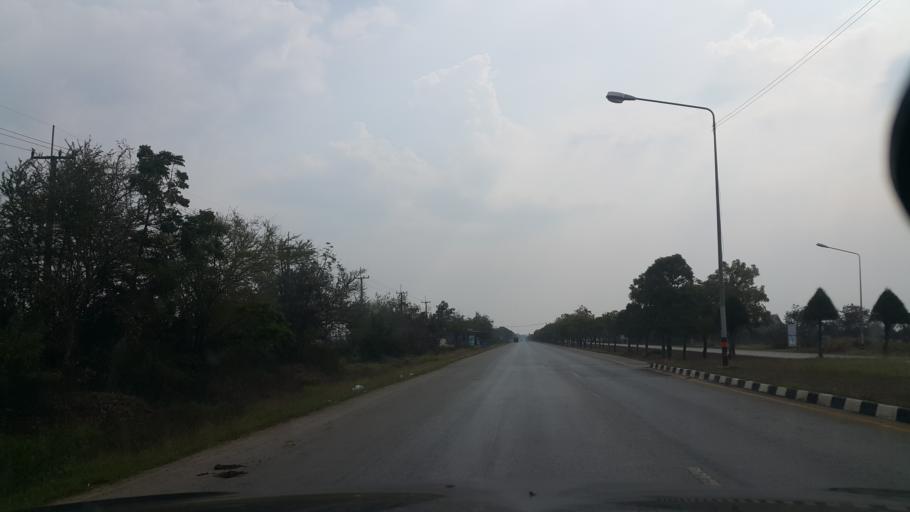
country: TH
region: Sukhothai
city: Sukhothai
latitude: 17.0637
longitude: 99.8786
